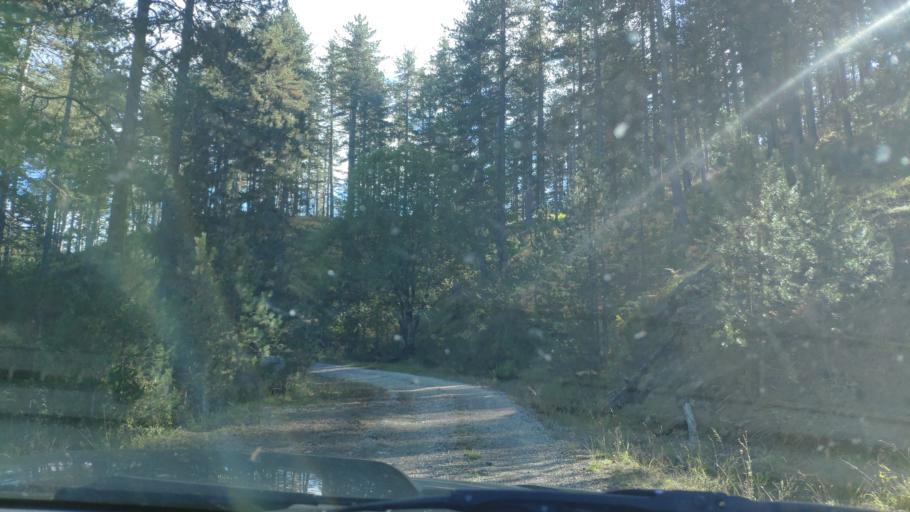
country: AL
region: Korce
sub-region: Rrethi i Devollit
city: Miras
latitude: 40.3944
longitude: 20.8858
